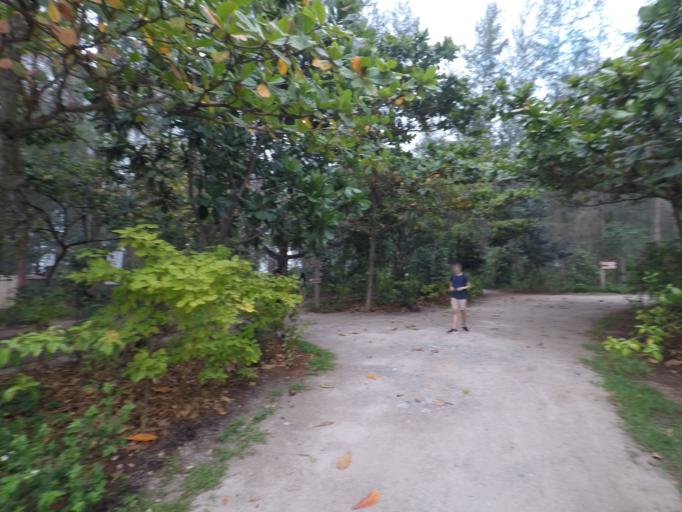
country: MY
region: Johor
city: Kampung Pasir Gudang Baru
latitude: 1.4162
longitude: 103.9152
